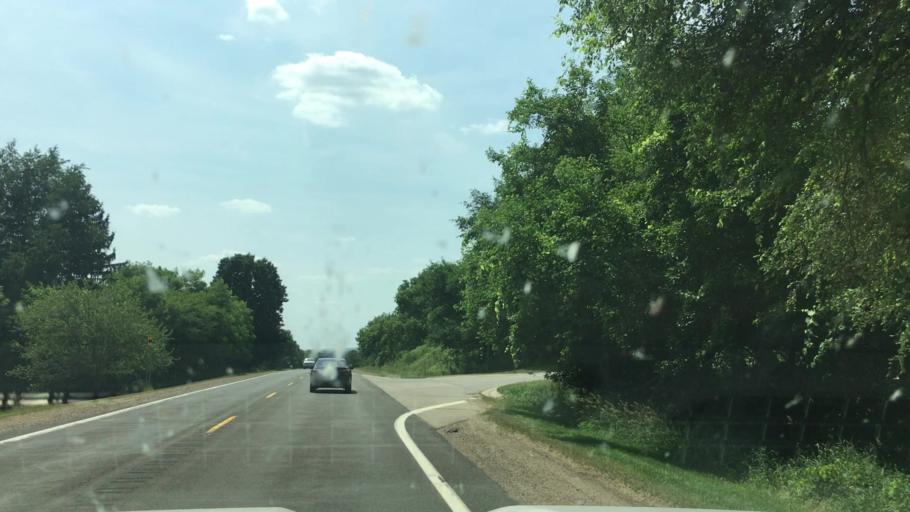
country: US
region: Michigan
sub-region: Allegan County
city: Plainwell
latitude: 42.4431
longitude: -85.5978
